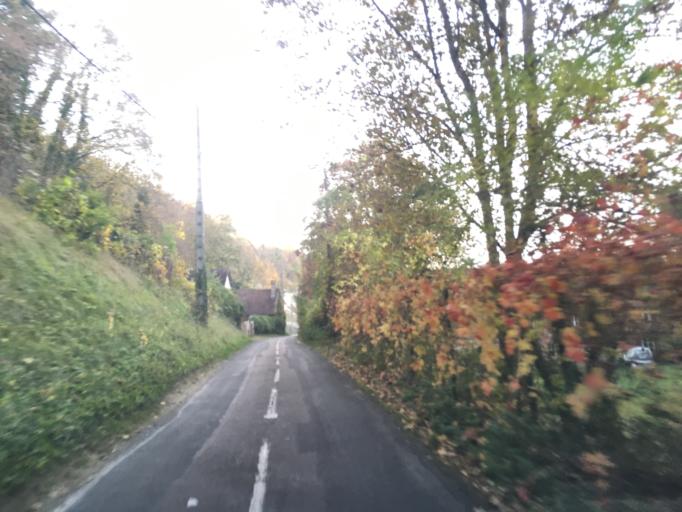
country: FR
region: Haute-Normandie
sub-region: Departement de l'Eure
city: Heudreville-sur-Eure
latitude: 49.1129
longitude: 1.2094
